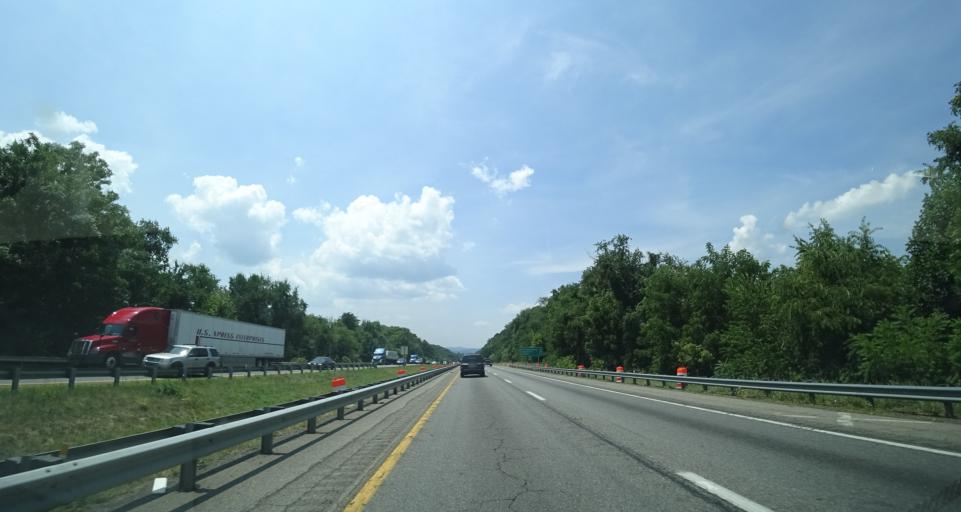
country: US
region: Virginia
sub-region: City of Salem
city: Salem
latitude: 37.3084
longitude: -80.0668
